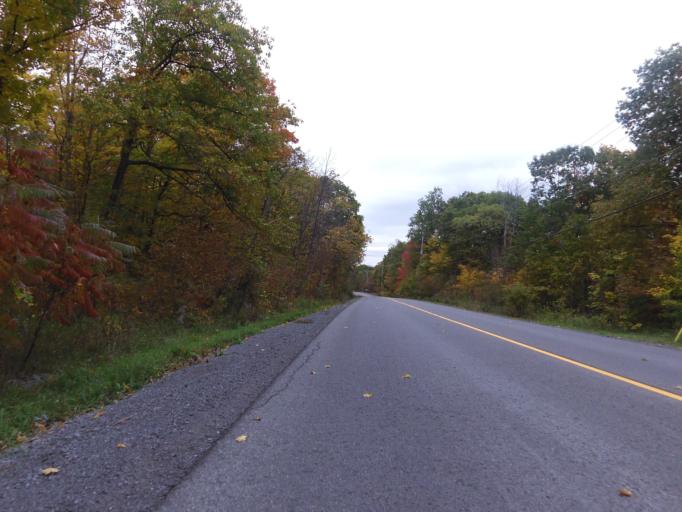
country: CA
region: Ontario
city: Arnprior
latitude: 45.4221
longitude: -76.0949
